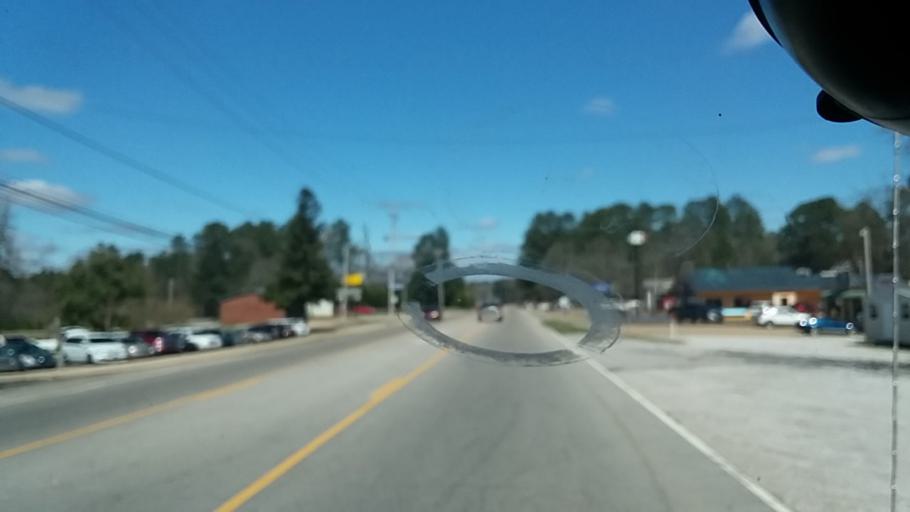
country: US
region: Mississippi
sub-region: Tishomingo County
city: Iuka
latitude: 34.8043
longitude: -88.2025
